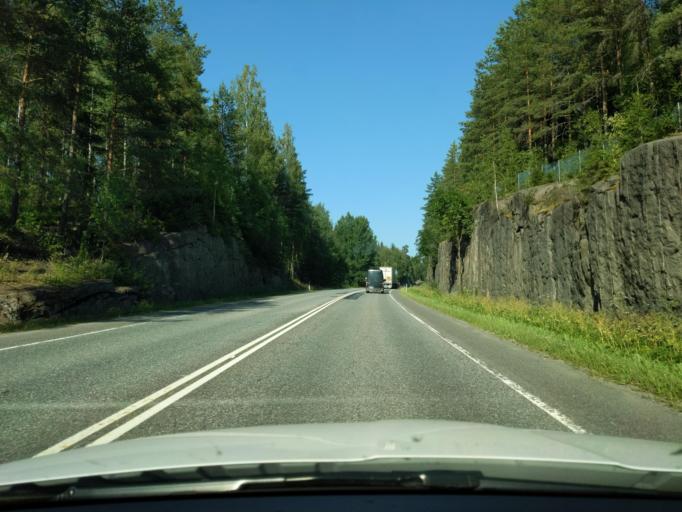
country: FI
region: Paijanne Tavastia
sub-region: Lahti
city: Hollola
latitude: 60.9713
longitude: 25.4709
